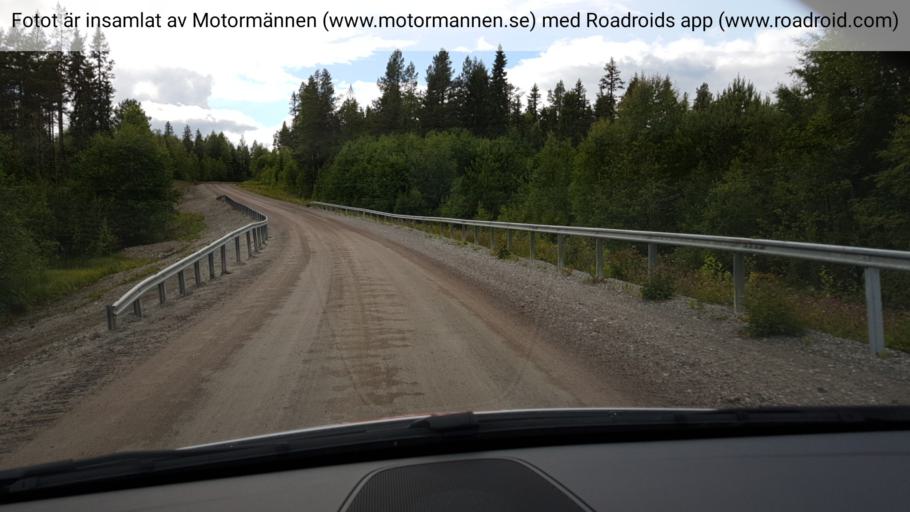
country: SE
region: Jaemtland
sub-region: Stroemsunds Kommun
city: Stroemsund
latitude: 64.0091
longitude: 15.9632
